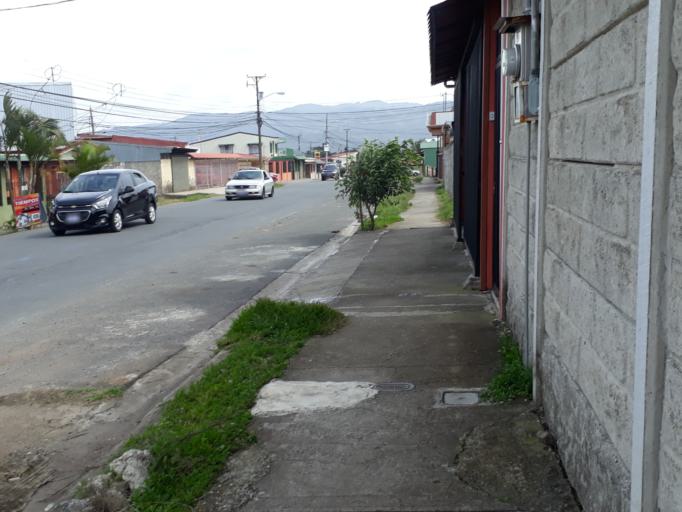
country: CR
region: Cartago
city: Cartago
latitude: 9.8747
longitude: -83.9410
